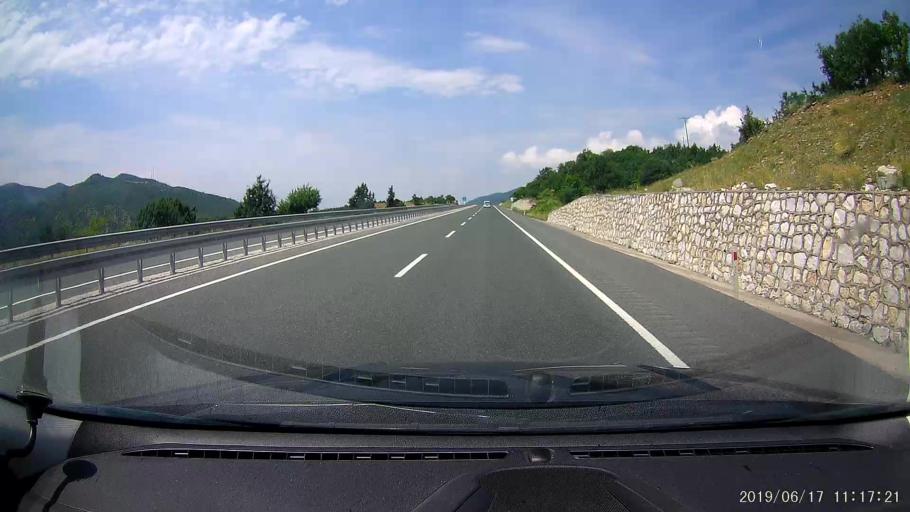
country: TR
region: Kastamonu
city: Tosya
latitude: 40.9419
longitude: 33.8771
